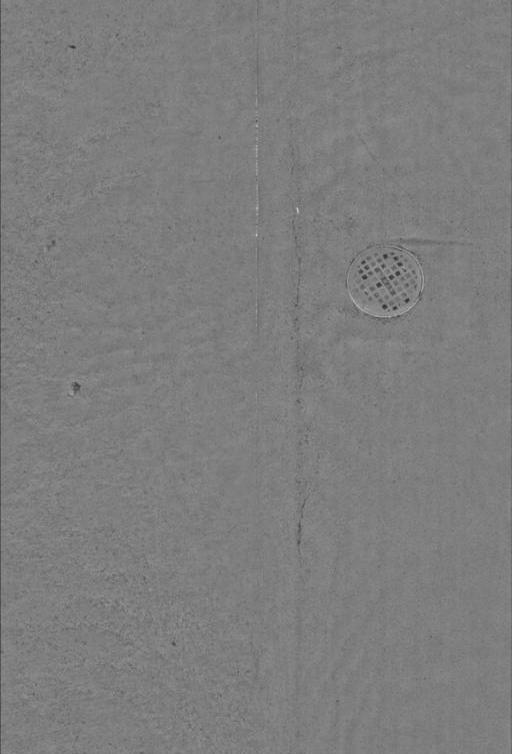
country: US
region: Maryland
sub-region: Montgomery County
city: Takoma Park
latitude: 38.9630
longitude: -77.0059
